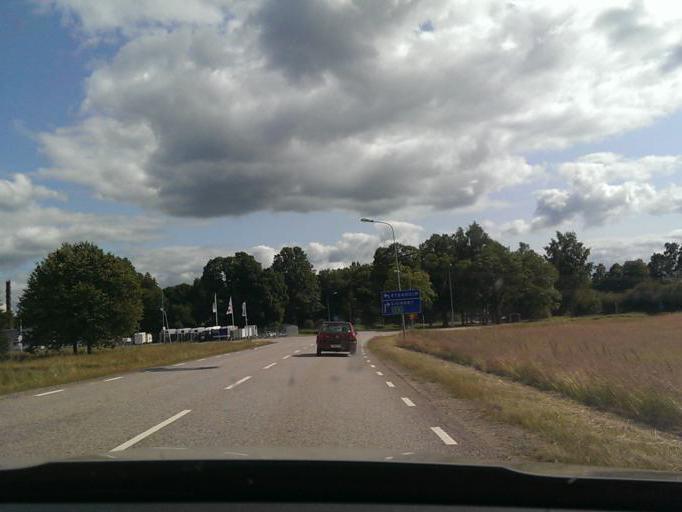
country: SE
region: Kronoberg
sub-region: Ljungby Kommun
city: Lagan
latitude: 56.9192
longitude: 13.9904
